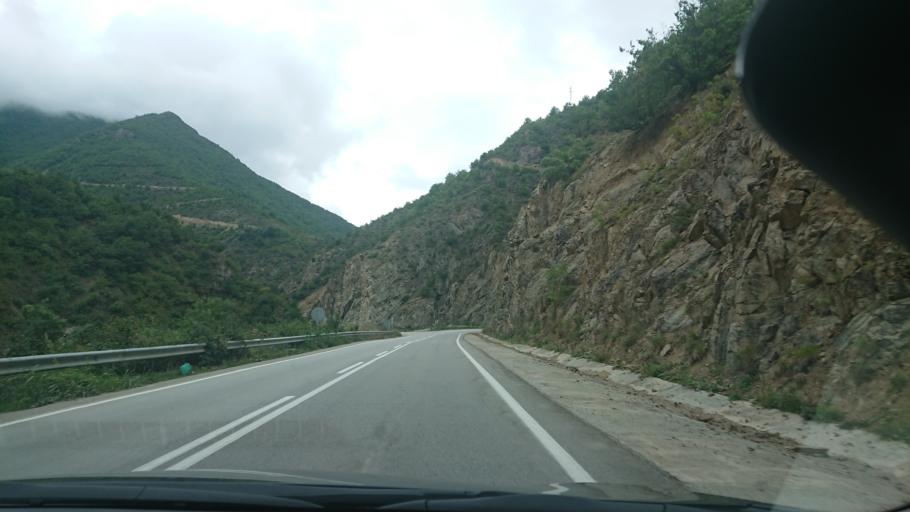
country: TR
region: Gumushane
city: Kurtun
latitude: 40.7047
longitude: 39.0720
